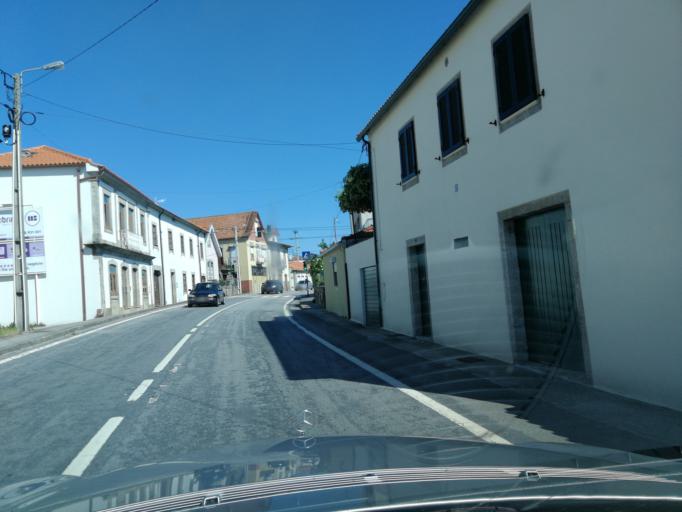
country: PT
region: Viana do Castelo
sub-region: Viana do Castelo
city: Meadela
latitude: 41.7066
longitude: -8.7936
